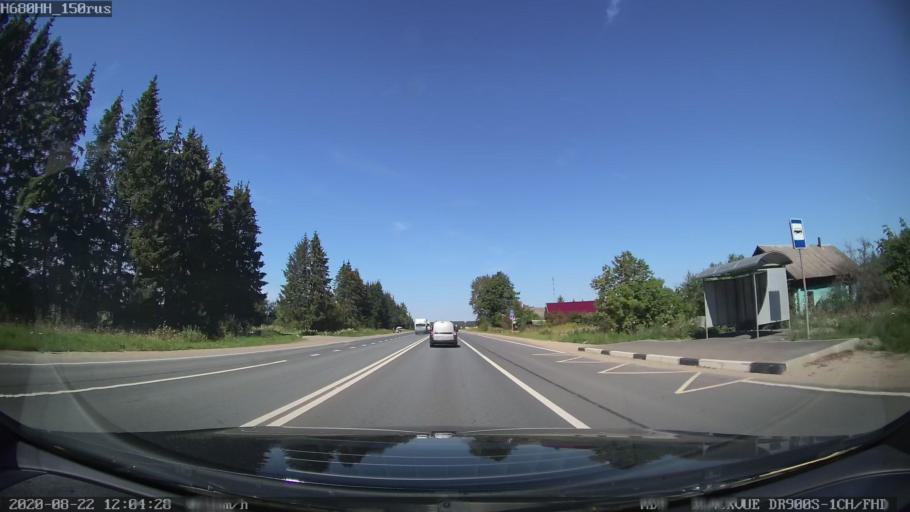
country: RU
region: Tverskaya
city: Rameshki
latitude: 57.2678
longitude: 36.0733
